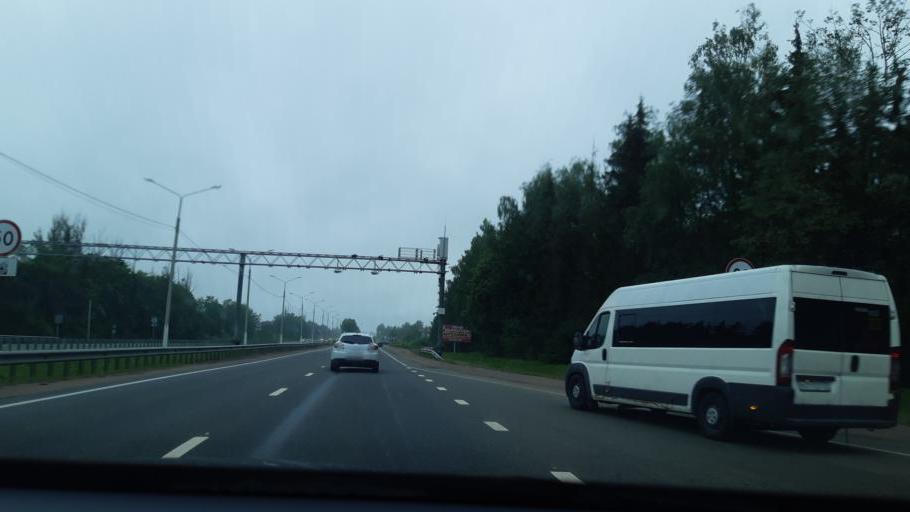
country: RU
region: Smolensk
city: Talashkino
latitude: 54.6816
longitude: 32.1400
